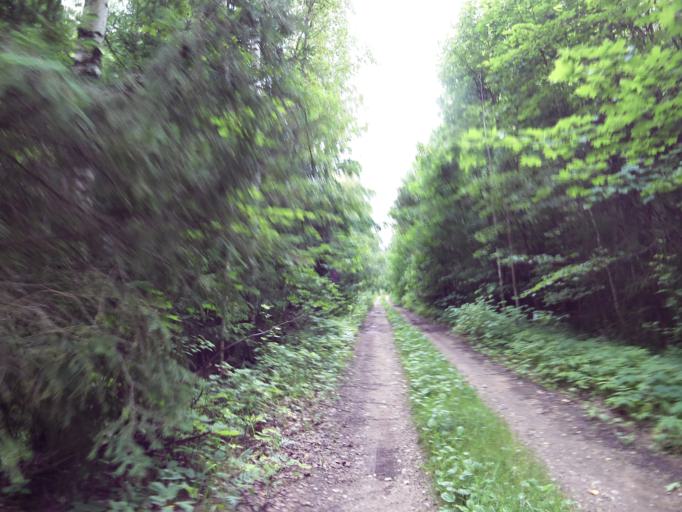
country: RU
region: Moskovskaya
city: Popovo
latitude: 54.9606
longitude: 37.7025
